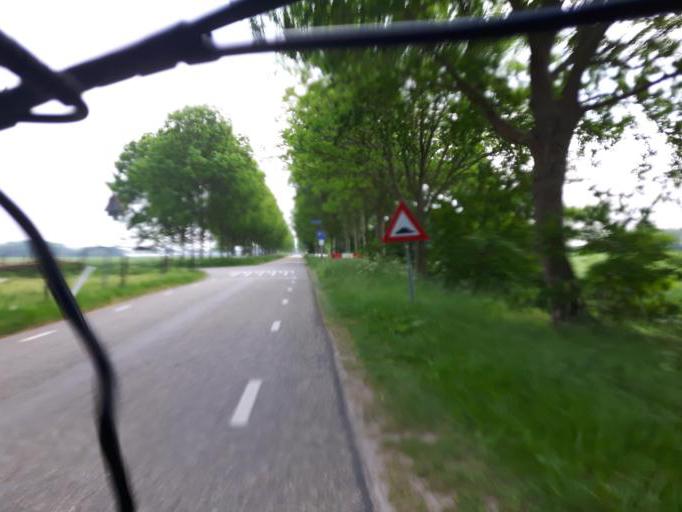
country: NL
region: North Brabant
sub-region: Gemeente Steenbergen
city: Welberg
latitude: 51.5537
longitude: 4.3546
